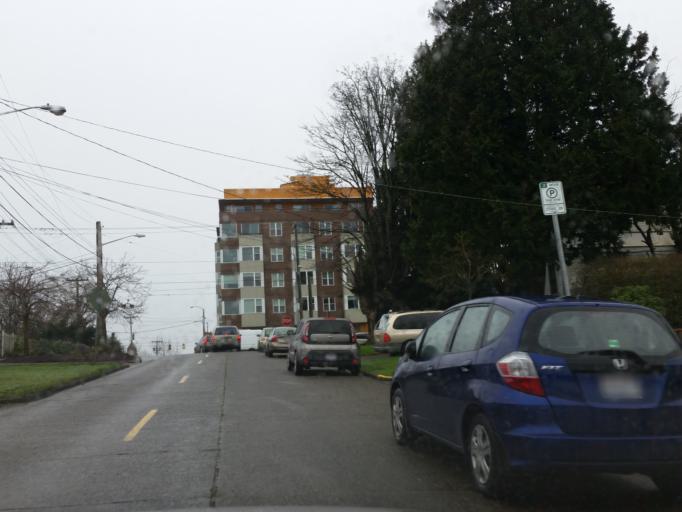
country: US
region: Washington
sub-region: King County
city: Seattle
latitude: 47.5788
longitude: -122.3099
